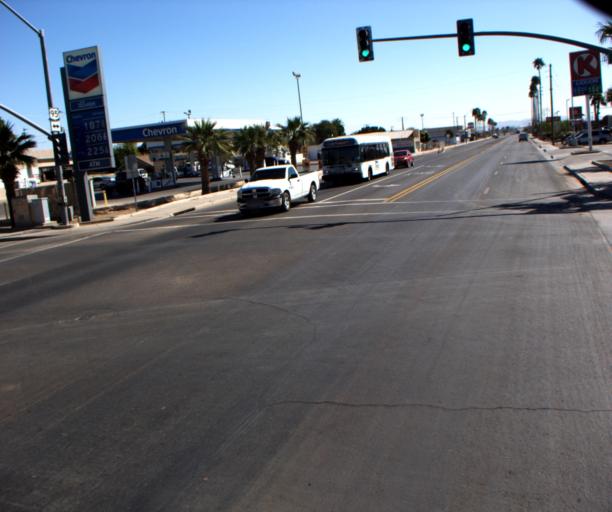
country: US
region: Arizona
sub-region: Yuma County
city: Somerton
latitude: 32.5966
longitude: -114.7099
